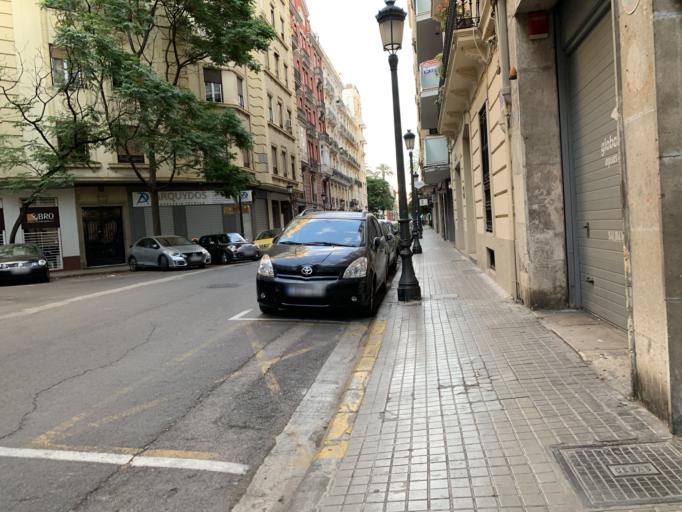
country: ES
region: Valencia
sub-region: Provincia de Valencia
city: Valencia
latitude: 39.4651
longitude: -0.3704
